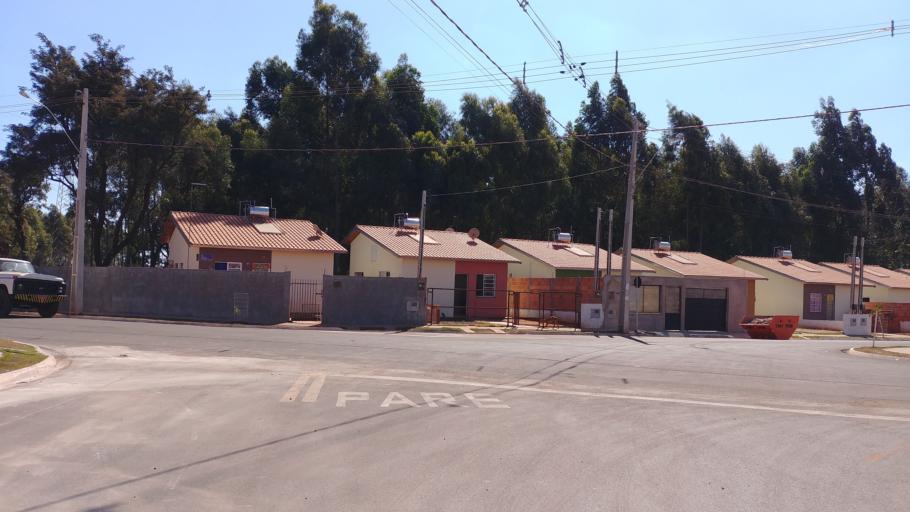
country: BR
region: Sao Paulo
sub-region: Paraguacu Paulista
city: Paraguacu Paulista
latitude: -22.4454
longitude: -50.5892
